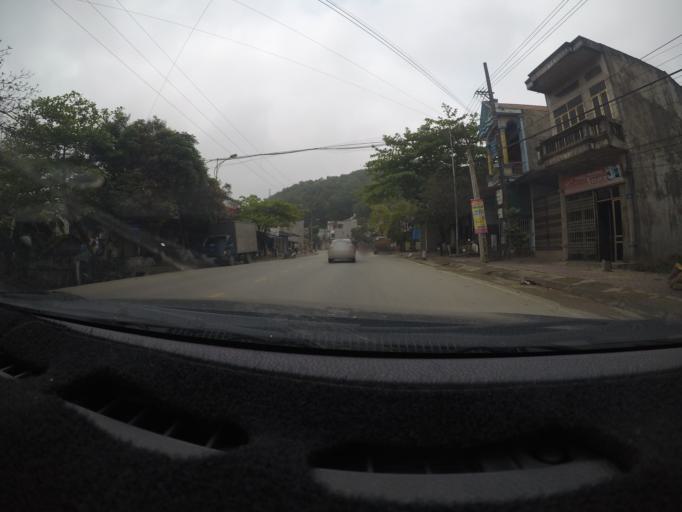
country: VN
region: Yen Bai
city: Yen Bai
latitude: 21.7333
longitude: 104.9552
